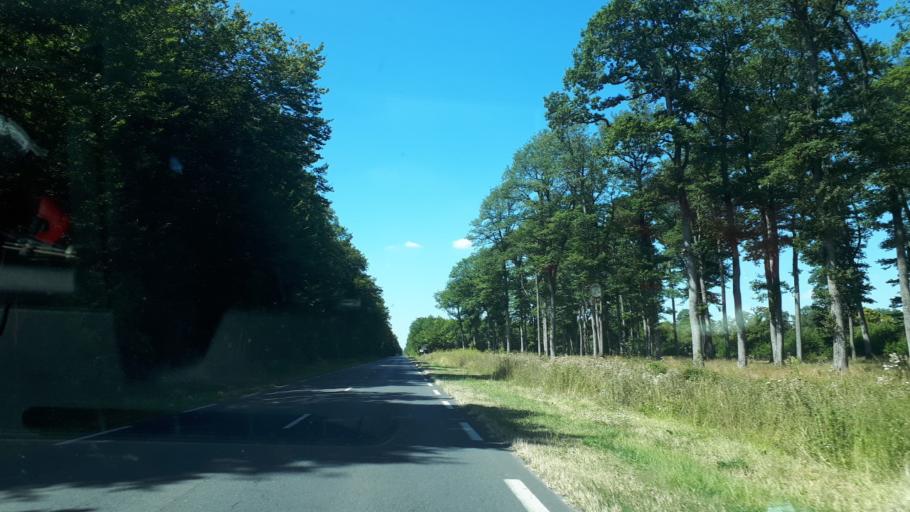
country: FR
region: Centre
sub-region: Departement du Loir-et-Cher
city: Mont-pres-Chambord
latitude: 47.5624
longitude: 1.4283
